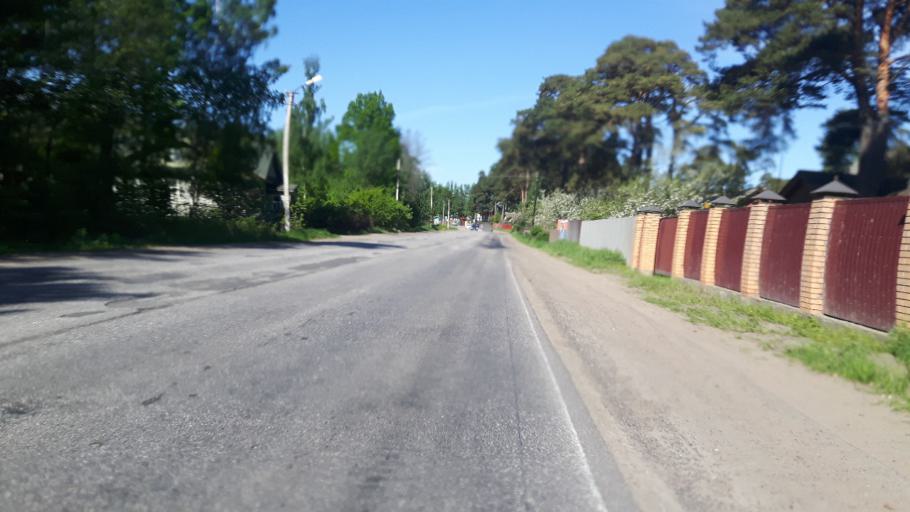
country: RU
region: Leningrad
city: Lebyazh'ye
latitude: 59.9600
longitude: 29.4355
